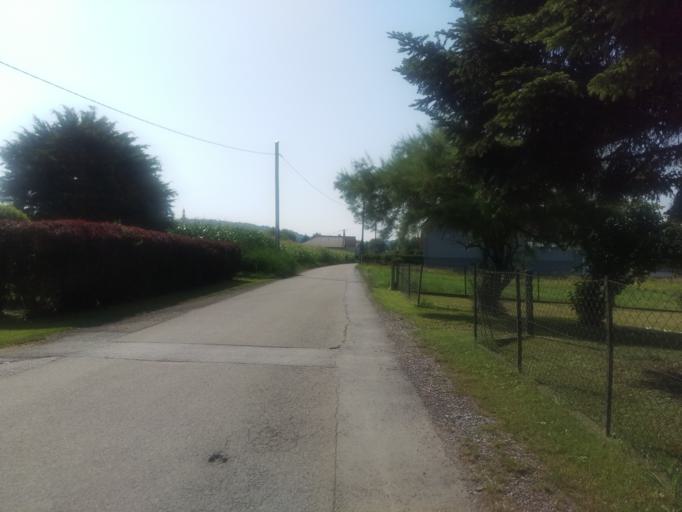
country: AT
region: Styria
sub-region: Politischer Bezirk Graz-Umgebung
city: Fernitz
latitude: 46.9778
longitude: 15.4920
